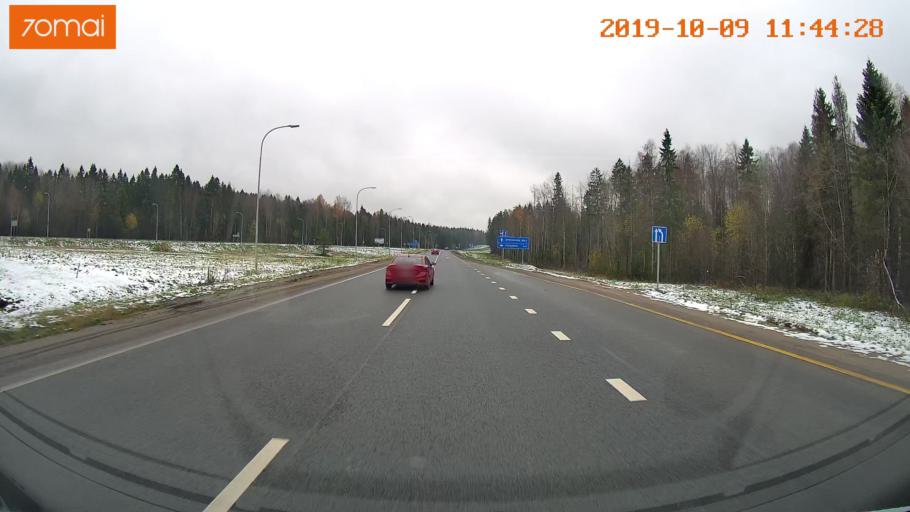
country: RU
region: Vologda
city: Gryazovets
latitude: 58.8828
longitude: 40.1910
